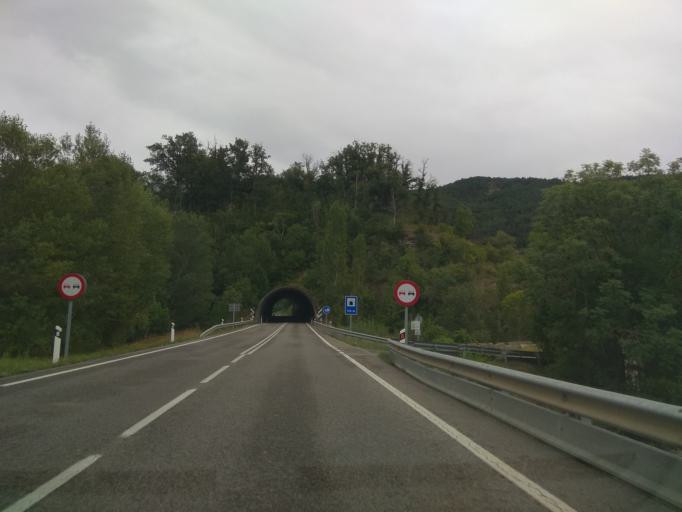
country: ES
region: Catalonia
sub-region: Provincia de Lleida
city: Alas i Cerc
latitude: 42.3578
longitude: 1.5203
